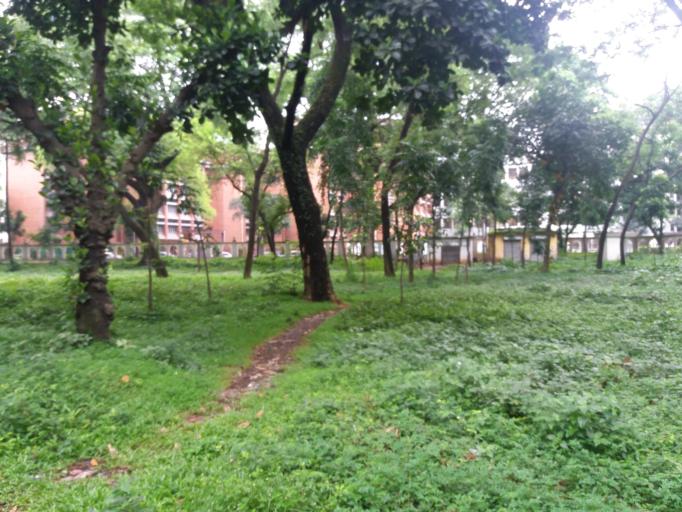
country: BD
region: Dhaka
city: Azimpur
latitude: 23.7287
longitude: 90.3916
